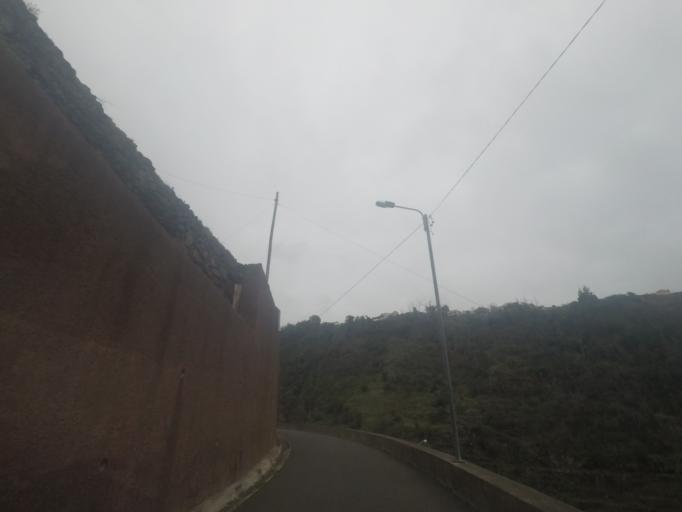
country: PT
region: Madeira
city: Camara de Lobos
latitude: 32.6652
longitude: -16.9616
